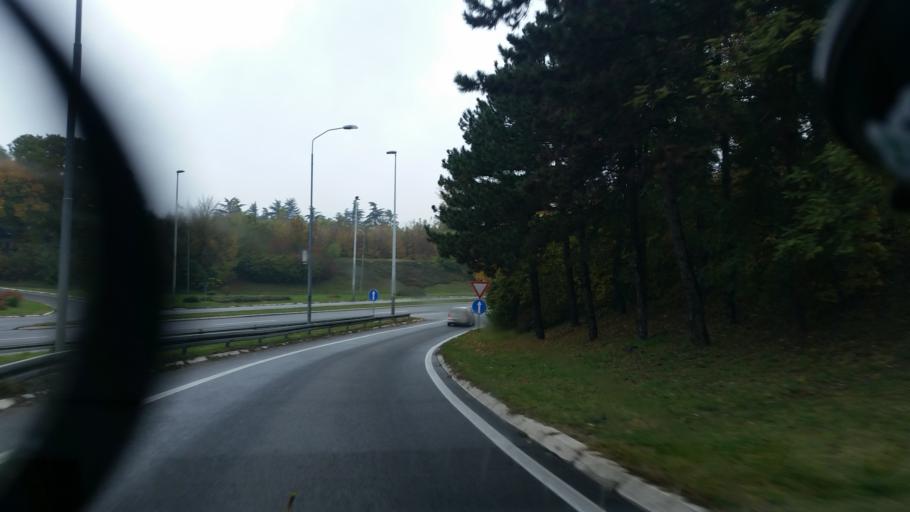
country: RS
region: Central Serbia
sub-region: Belgrade
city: Zemun
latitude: 44.8326
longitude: 20.3641
